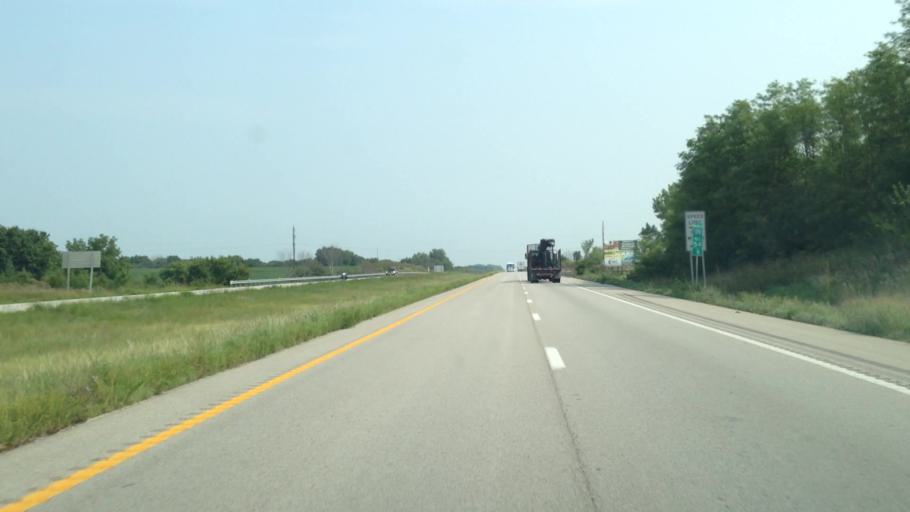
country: US
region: Missouri
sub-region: Clinton County
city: Cameron
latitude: 39.7615
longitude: -94.2174
